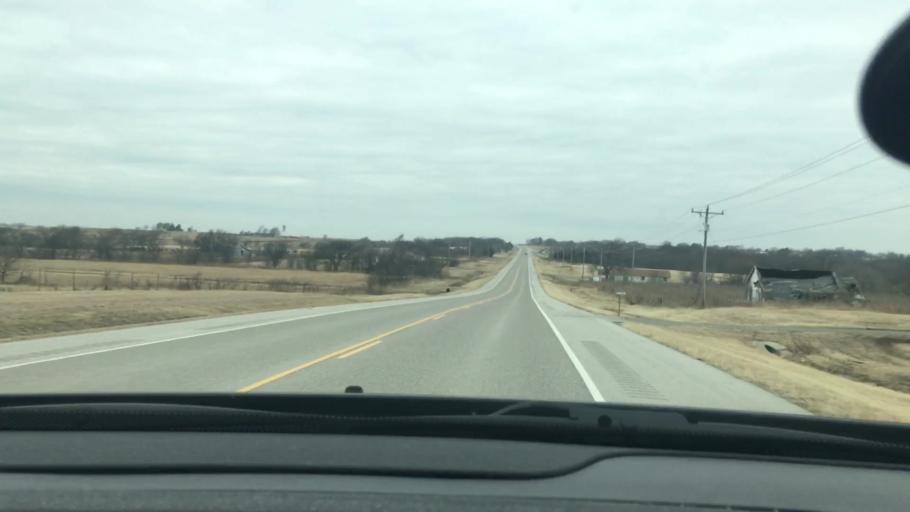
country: US
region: Oklahoma
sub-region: Garvin County
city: Wynnewood
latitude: 34.5123
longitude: -97.3405
